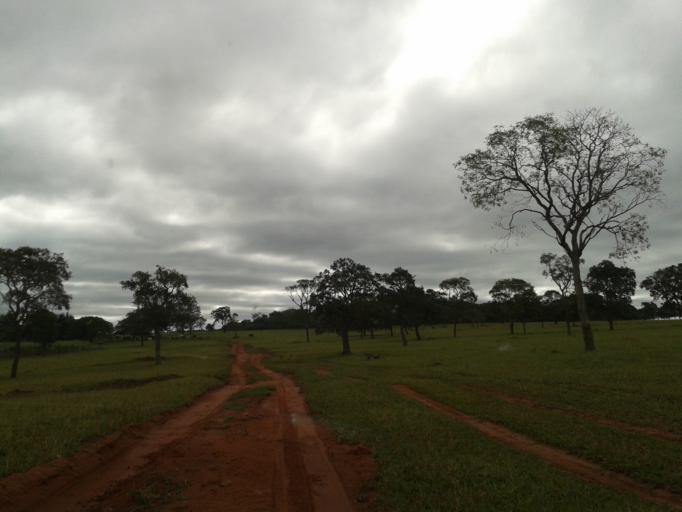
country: BR
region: Minas Gerais
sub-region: Campina Verde
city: Campina Verde
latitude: -19.4945
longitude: -49.6646
